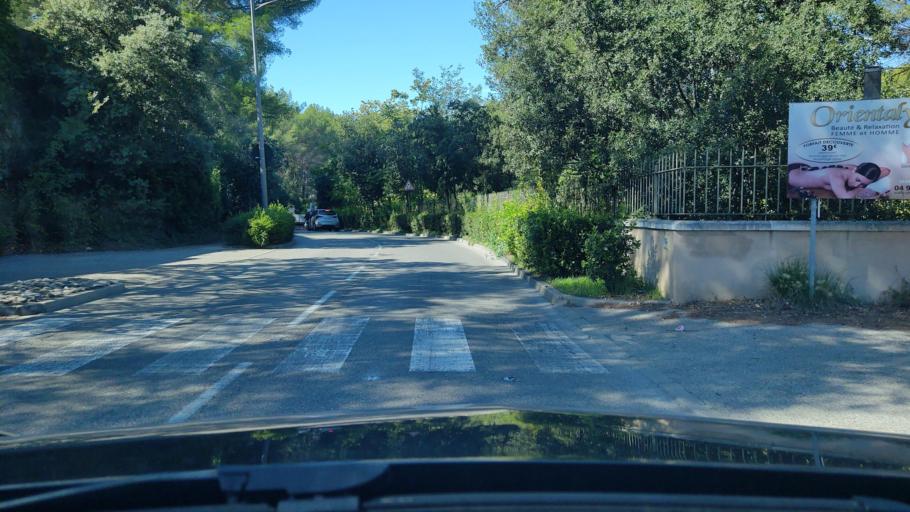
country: FR
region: Provence-Alpes-Cote d'Azur
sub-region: Departement du Var
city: Sanary-sur-Mer
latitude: 43.1442
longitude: 5.7726
